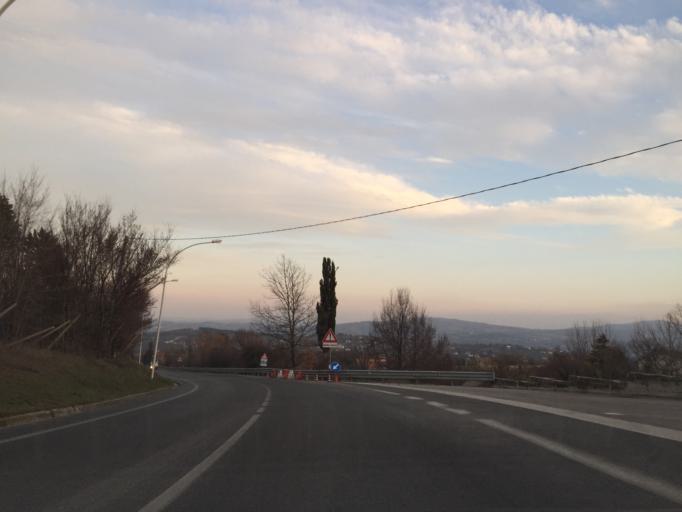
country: IT
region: Molise
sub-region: Provincia di Campobasso
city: Campobasso
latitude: 41.5617
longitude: 14.6860
